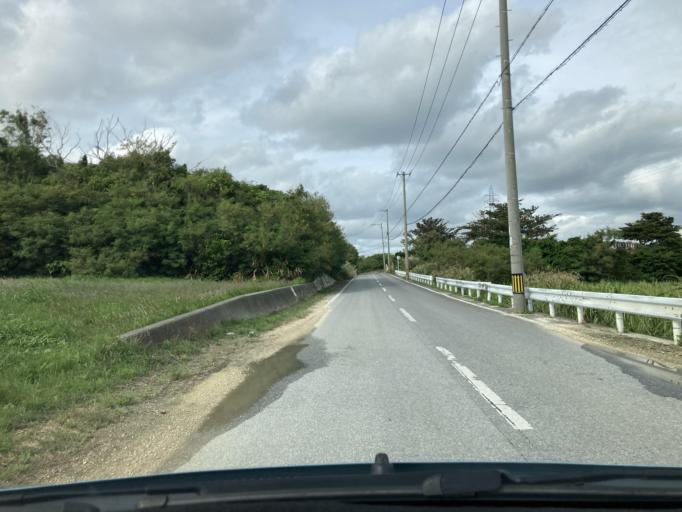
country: JP
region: Okinawa
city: Itoman
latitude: 26.1129
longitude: 127.6888
